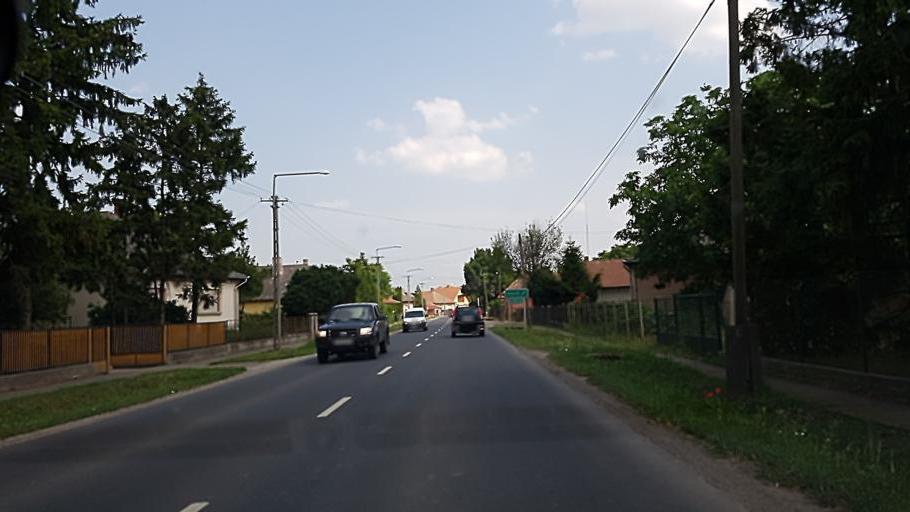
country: HU
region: Heves
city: Besenyotelek
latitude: 47.6973
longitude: 20.4299
